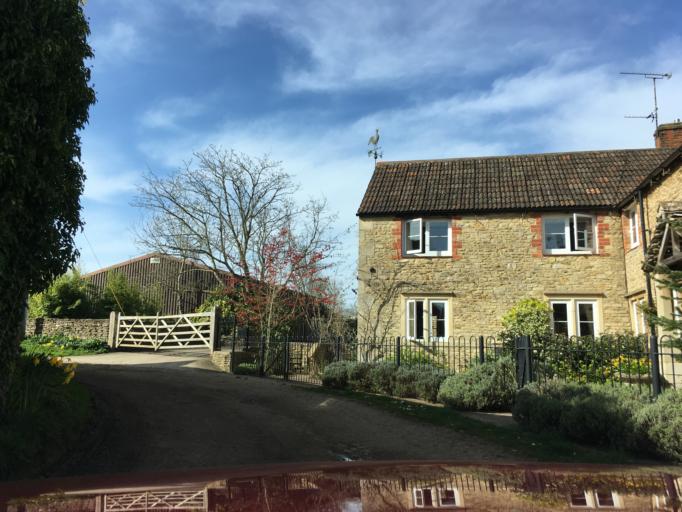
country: GB
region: England
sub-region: Wiltshire
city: Chippenham
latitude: 51.4944
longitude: -2.1400
